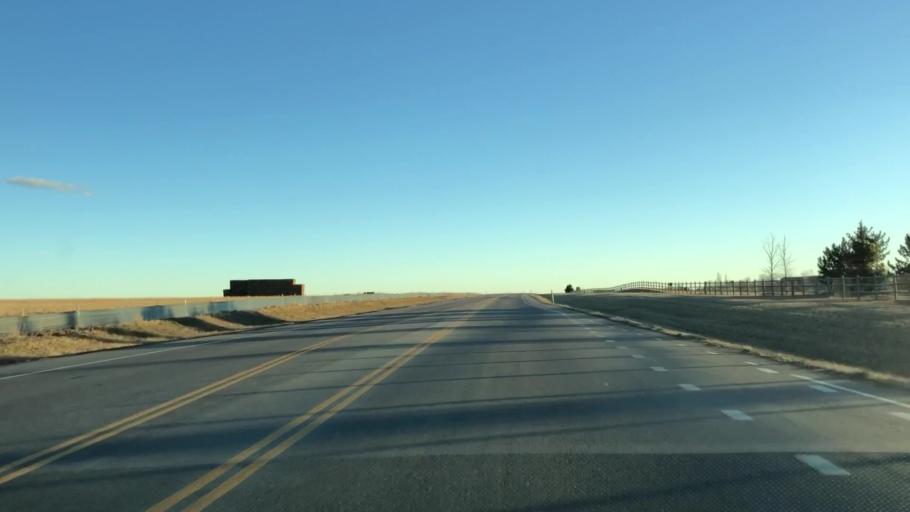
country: US
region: Colorado
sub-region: Weld County
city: Windsor
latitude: 40.4442
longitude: -104.9443
